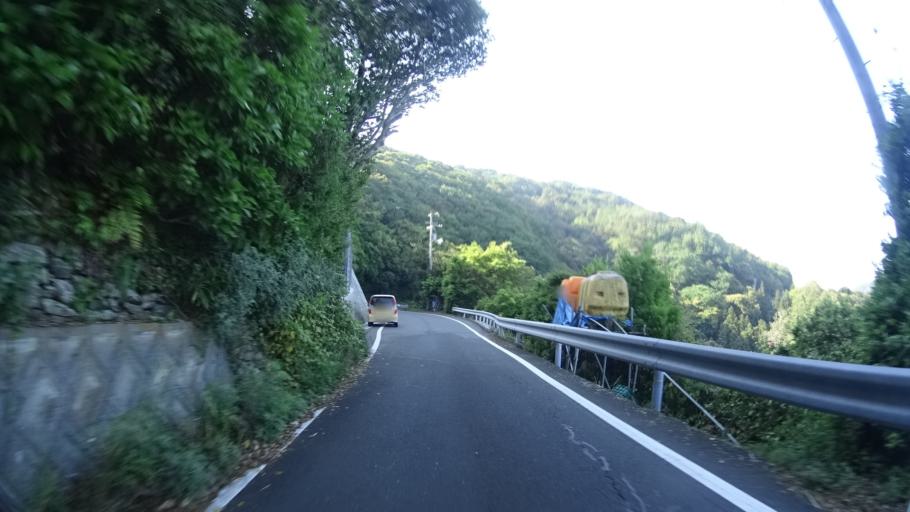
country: JP
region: Oita
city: Tsukumiura
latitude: 33.3558
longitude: 132.0316
